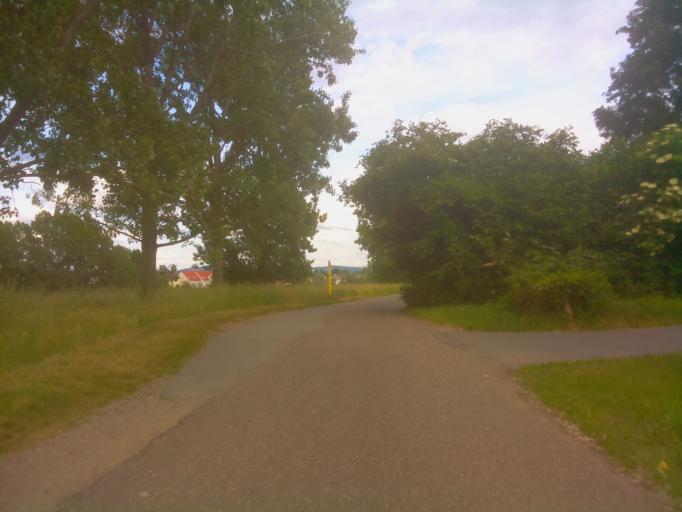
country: DE
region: Baden-Wuerttemberg
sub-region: Karlsruhe Region
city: Ilvesheim
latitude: 49.4748
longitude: 8.5553
